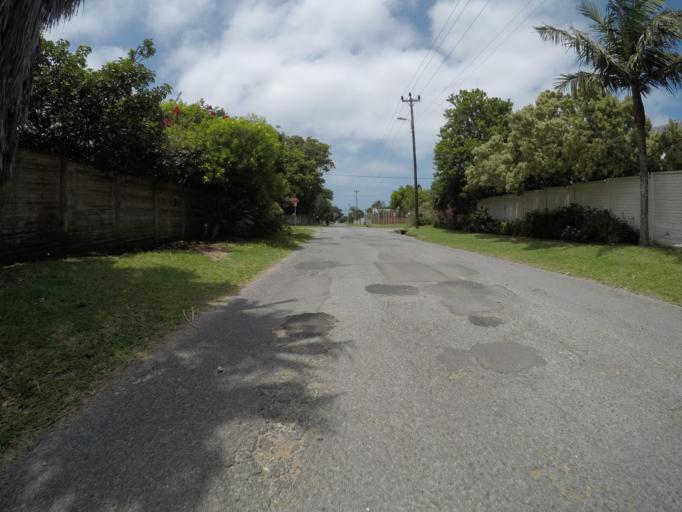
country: ZA
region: Eastern Cape
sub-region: Buffalo City Metropolitan Municipality
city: East London
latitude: -32.9418
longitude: 28.0145
